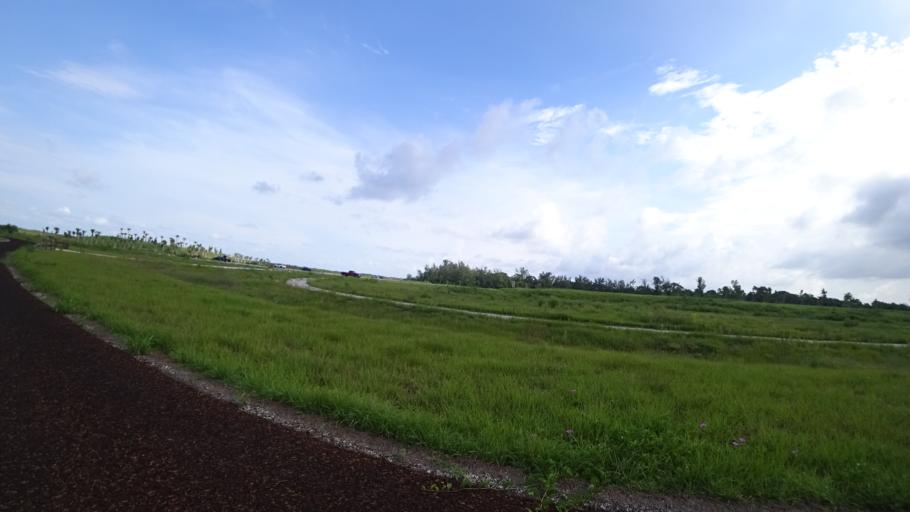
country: US
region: Florida
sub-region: Manatee County
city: Cortez
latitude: 27.5079
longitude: -82.6641
